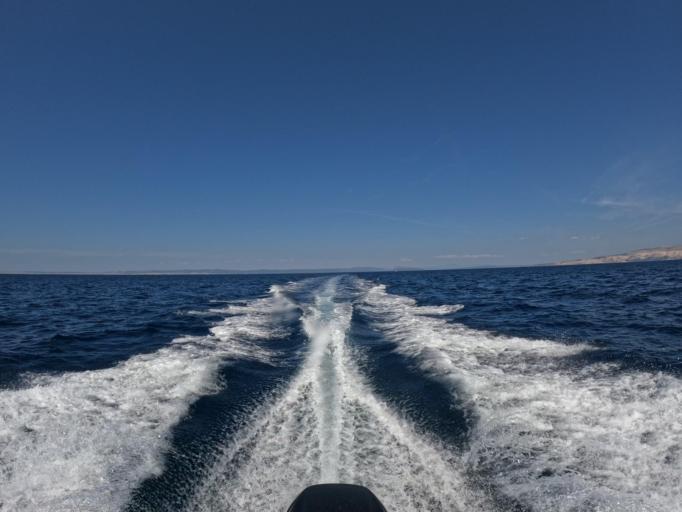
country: HR
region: Primorsko-Goranska
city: Lopar
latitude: 44.8604
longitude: 14.6917
